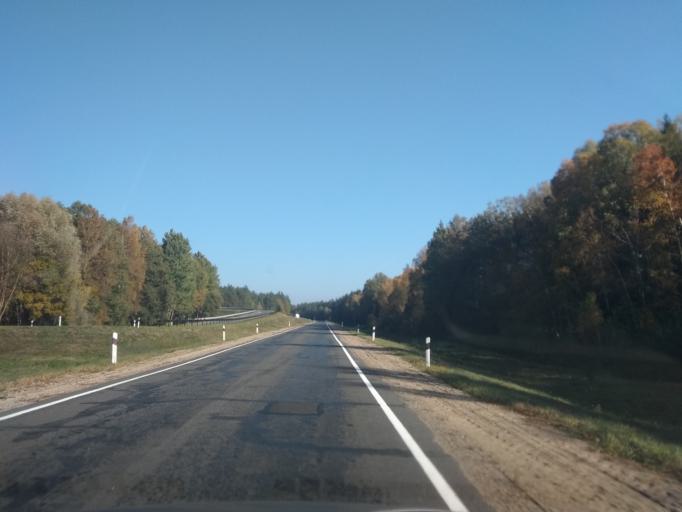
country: BY
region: Brest
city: Ivatsevichy
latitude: 52.8534
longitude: 25.6444
